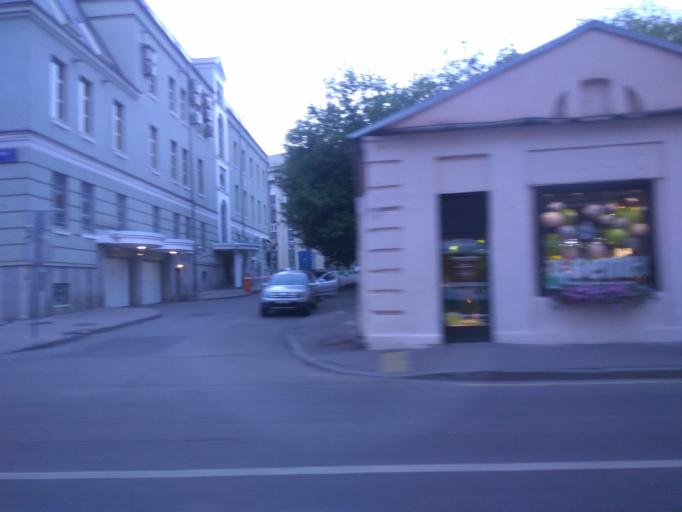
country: RU
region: Moscow
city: Lefortovo
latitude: 55.7699
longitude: 37.6702
